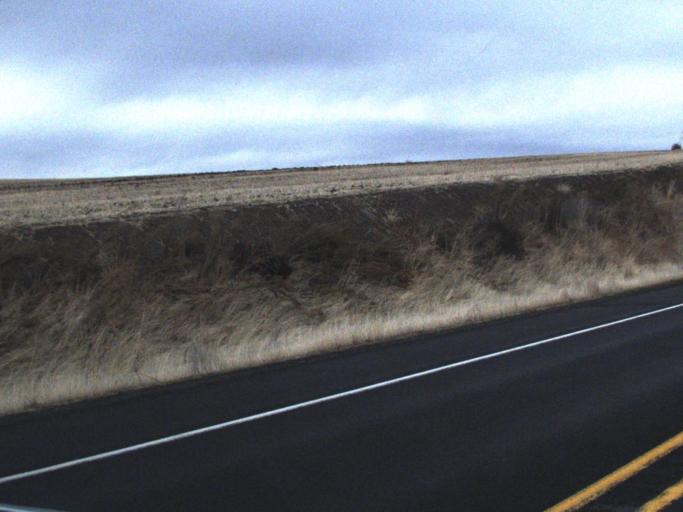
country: US
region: Washington
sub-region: Walla Walla County
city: Walla Walla East
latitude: 46.1153
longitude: -118.2231
